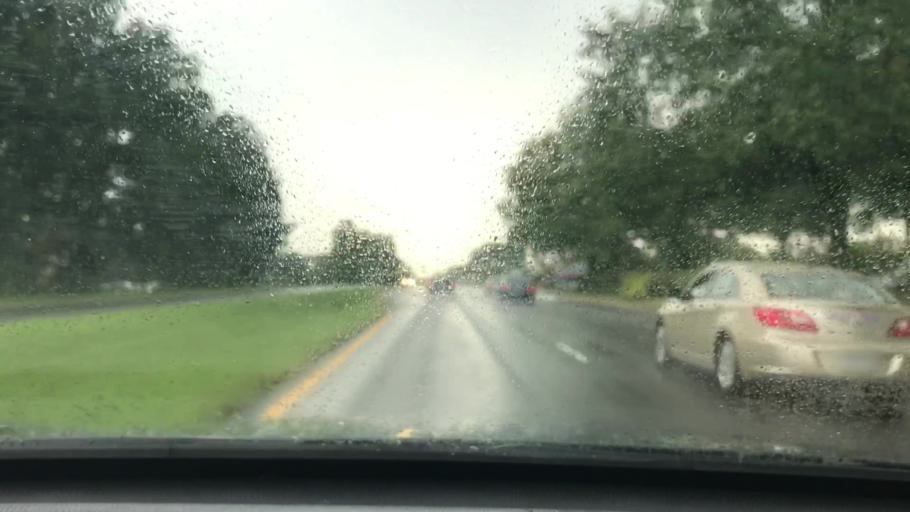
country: US
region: Virginia
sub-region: Henrico County
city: Laurel
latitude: 37.6301
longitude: -77.5253
